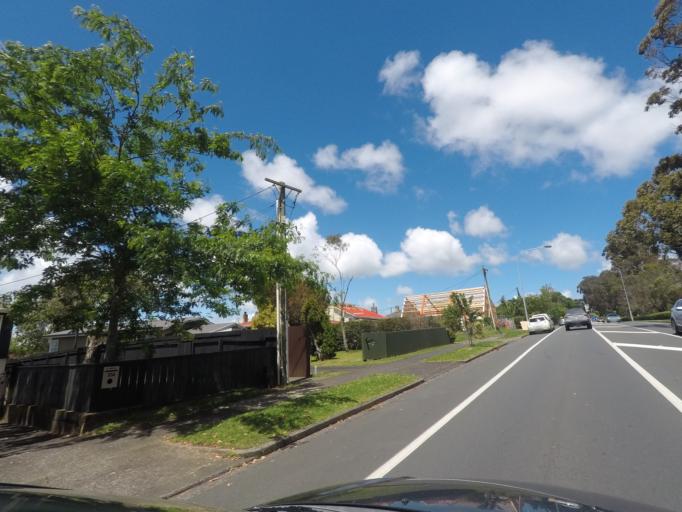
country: NZ
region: Auckland
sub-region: Auckland
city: Waitakere
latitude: -36.9050
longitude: 174.6534
